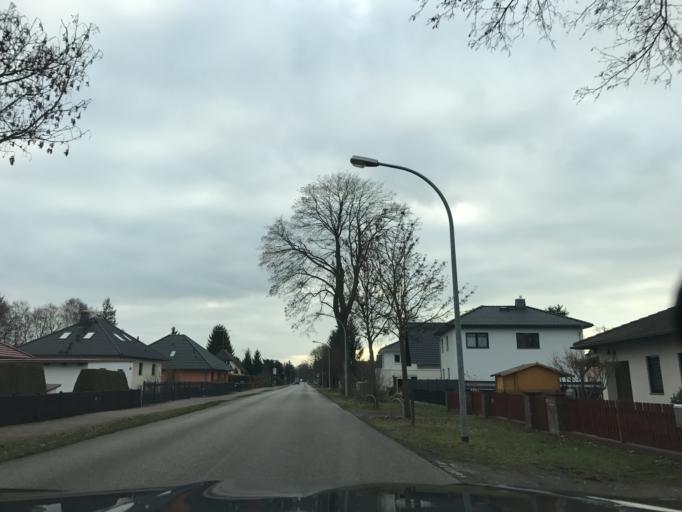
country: DE
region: Brandenburg
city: Brandenburg an der Havel
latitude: 52.3792
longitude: 12.5452
